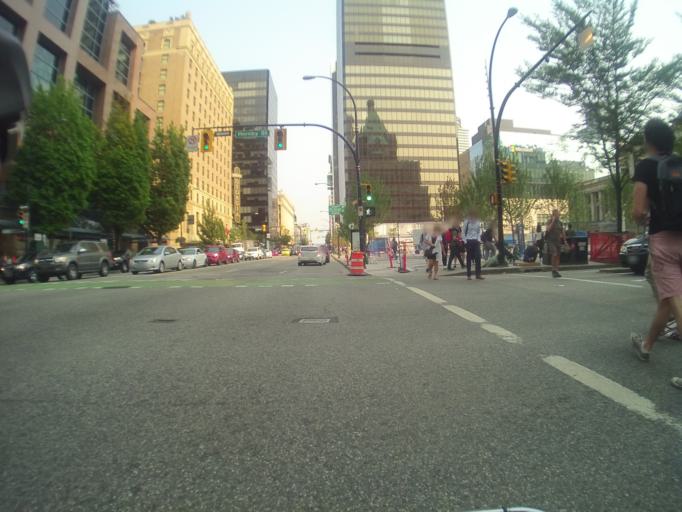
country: CA
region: British Columbia
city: West End
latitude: 49.2838
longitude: -123.1203
